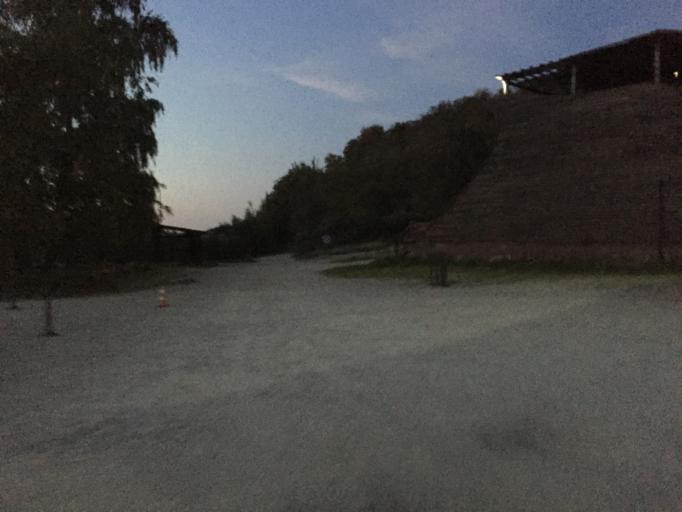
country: RU
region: Kaliningrad
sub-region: Gorod Kaliningrad
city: Yantarnyy
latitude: 54.8843
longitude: 19.9349
